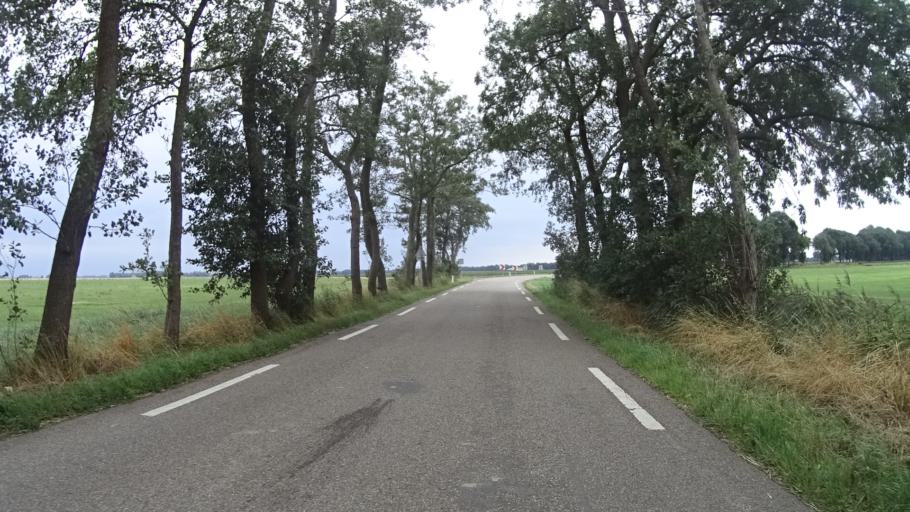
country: NL
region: Groningen
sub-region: Gemeente Slochteren
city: Slochteren
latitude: 53.2060
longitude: 6.8365
